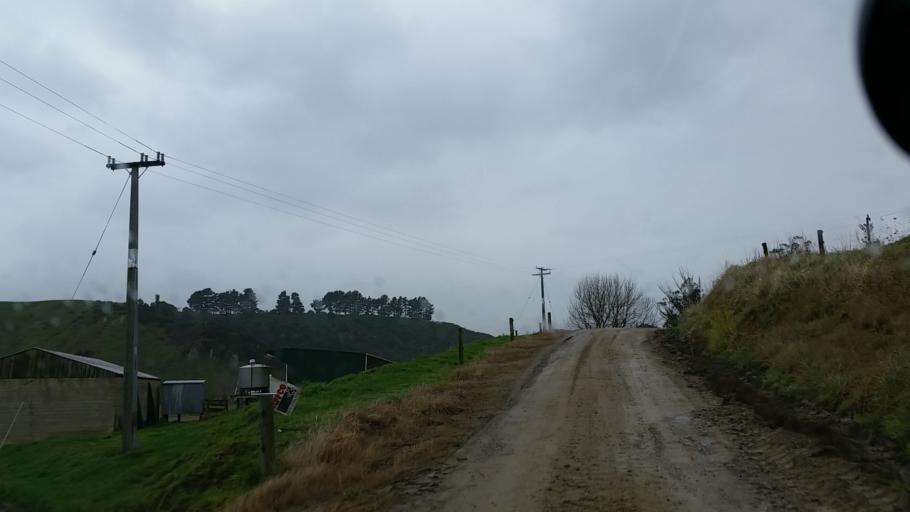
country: NZ
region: Taranaki
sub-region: South Taranaki District
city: Patea
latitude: -39.7574
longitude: 174.7108
